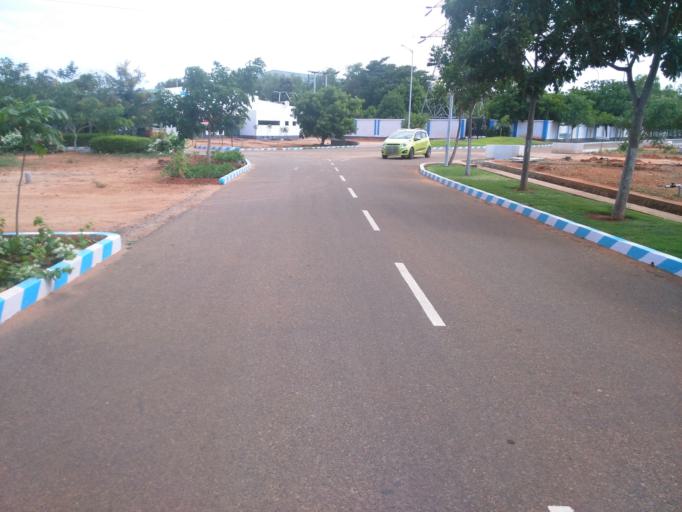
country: IN
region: Tamil Nadu
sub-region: Coimbatore
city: Sulur
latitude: 11.0773
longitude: 77.1414
